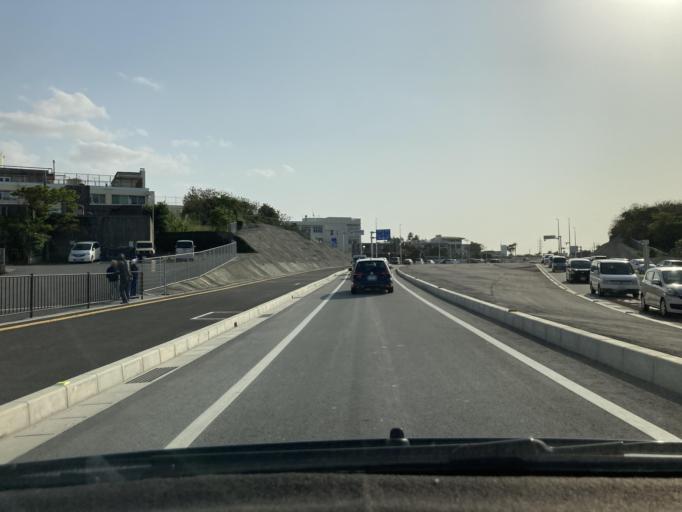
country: JP
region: Okinawa
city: Ginowan
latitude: 26.2038
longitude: 127.7485
